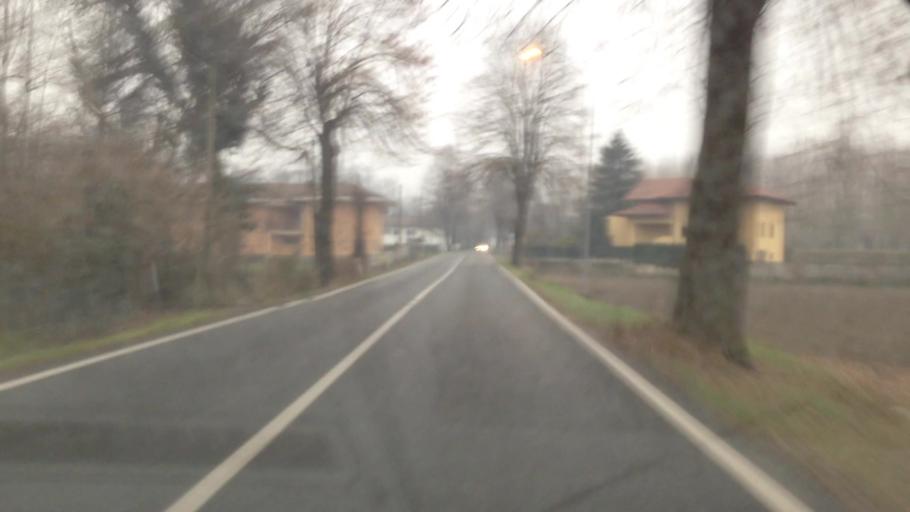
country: IT
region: Piedmont
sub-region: Provincia di Torino
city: Verrua Savoia
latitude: 45.1691
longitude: 8.0904
